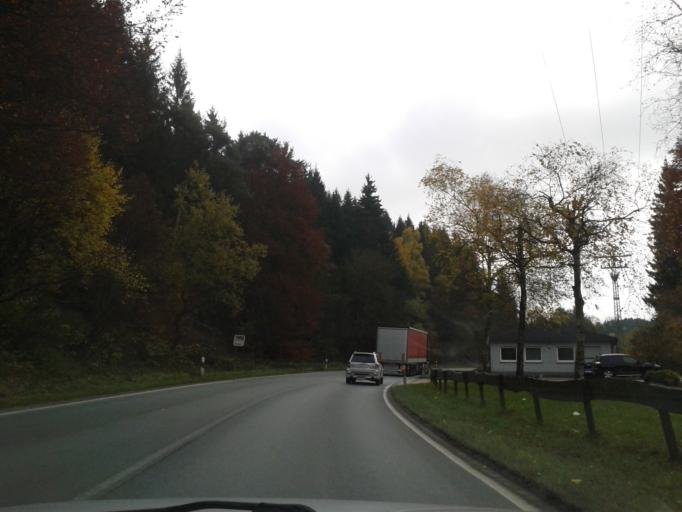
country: DE
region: North Rhine-Westphalia
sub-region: Regierungsbezirk Arnsberg
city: Bad Berleburg
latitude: 51.0208
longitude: 8.3724
